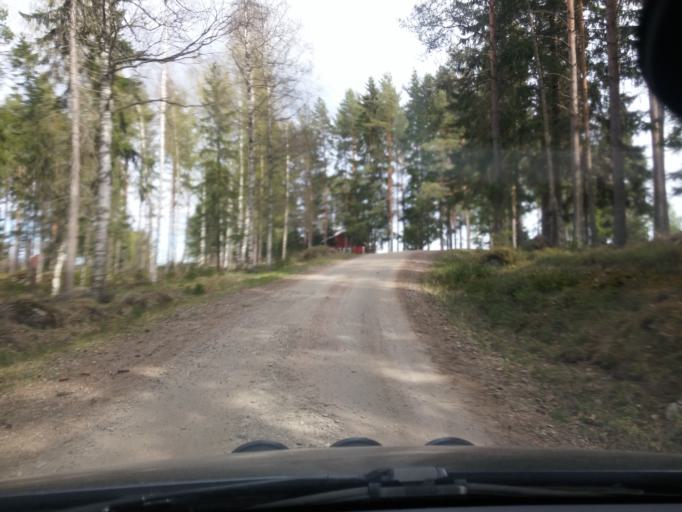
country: SE
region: Gaevleborg
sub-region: Ljusdals Kommun
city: Farila
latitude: 61.7903
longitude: 15.8941
